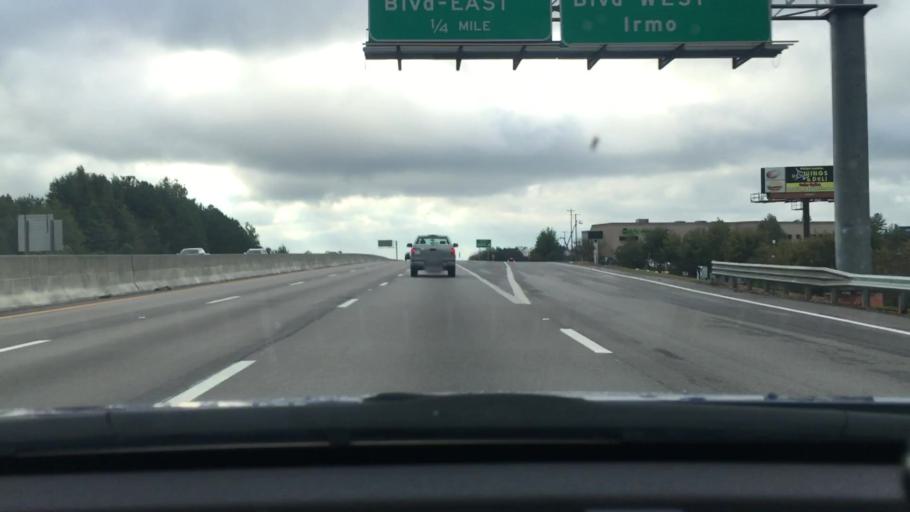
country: US
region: South Carolina
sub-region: Lexington County
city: Irmo
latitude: 34.0947
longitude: -81.1701
